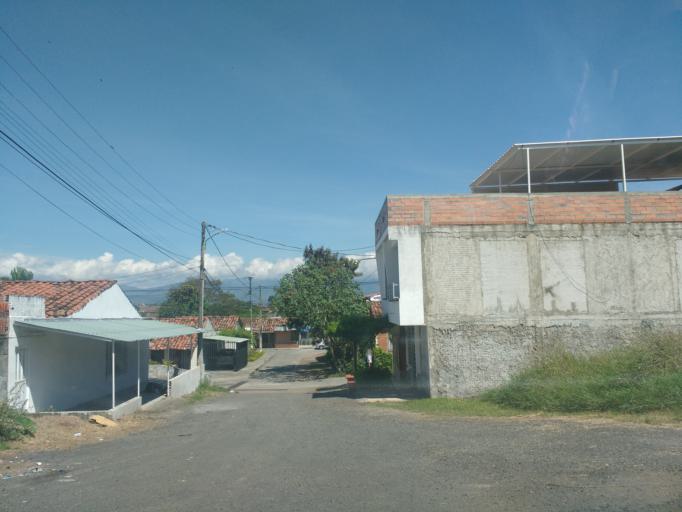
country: CO
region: Valle del Cauca
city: Cartago
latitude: 4.7515
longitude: -75.8988
